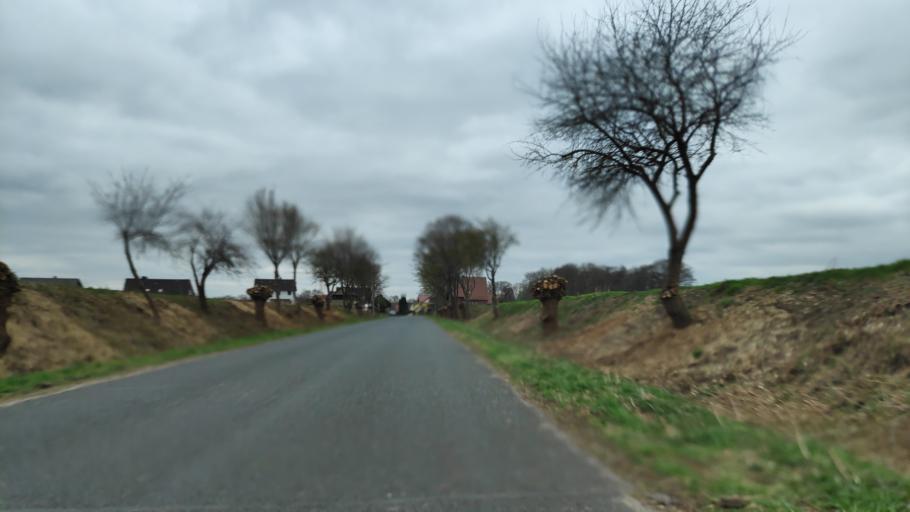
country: DE
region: North Rhine-Westphalia
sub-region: Regierungsbezirk Detmold
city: Petershagen
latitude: 52.3487
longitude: 8.9305
